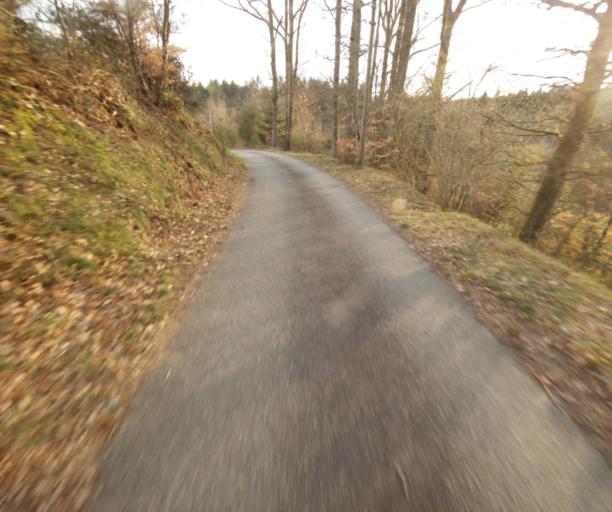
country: FR
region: Limousin
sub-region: Departement de la Correze
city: Argentat
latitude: 45.2447
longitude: 1.9580
